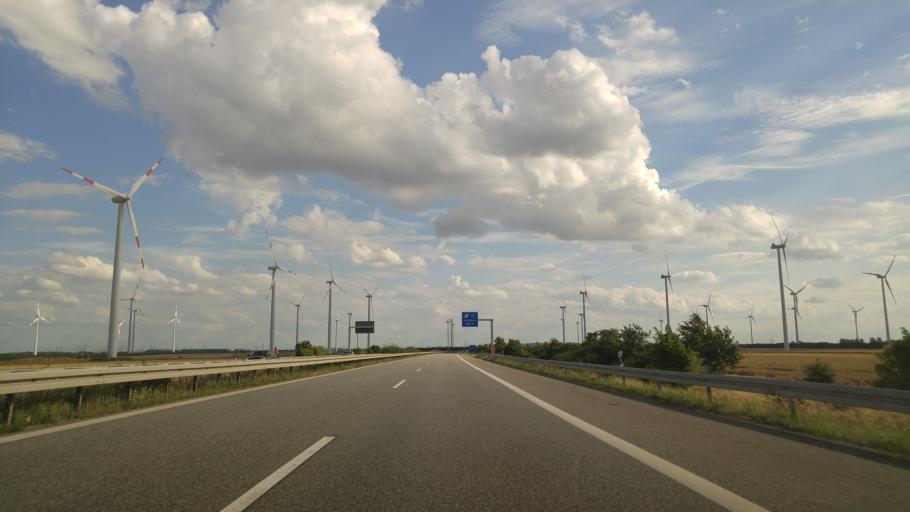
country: DE
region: Saxony-Anhalt
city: Zscherben
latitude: 51.4406
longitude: 11.8644
